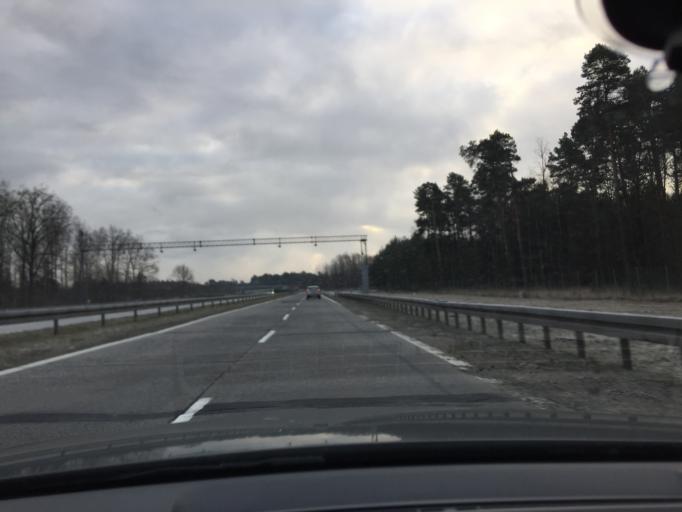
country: PL
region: Lubusz
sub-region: Powiat zarski
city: Lipinki Luzyckie
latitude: 51.5979
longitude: 14.9957
